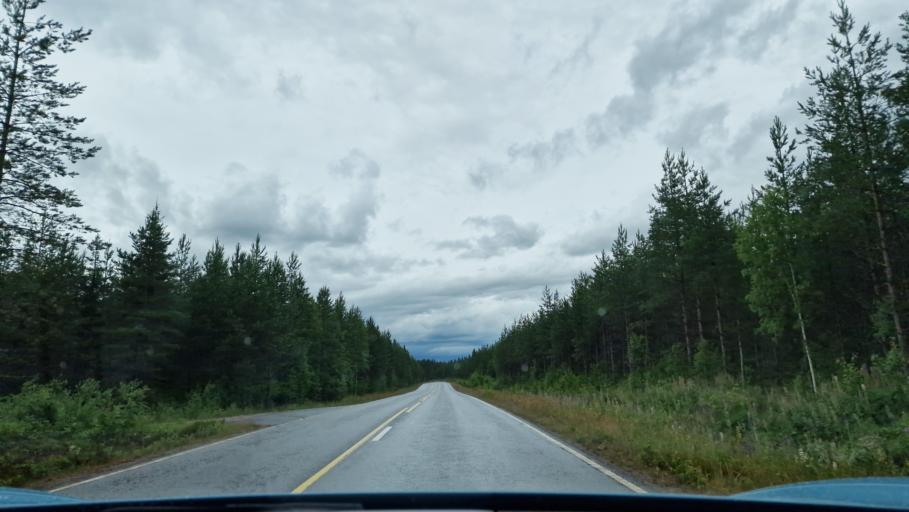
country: FI
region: Central Finland
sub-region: Saarijaervi-Viitasaari
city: Pylkoenmaeki
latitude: 62.6659
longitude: 24.5404
